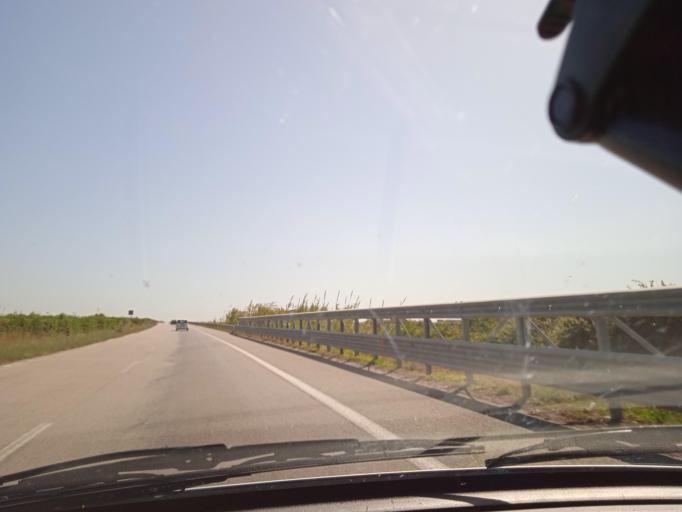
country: IT
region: Sicily
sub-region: Messina
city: Barcellona Pozzo di Gotto
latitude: 38.1604
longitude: 15.1962
